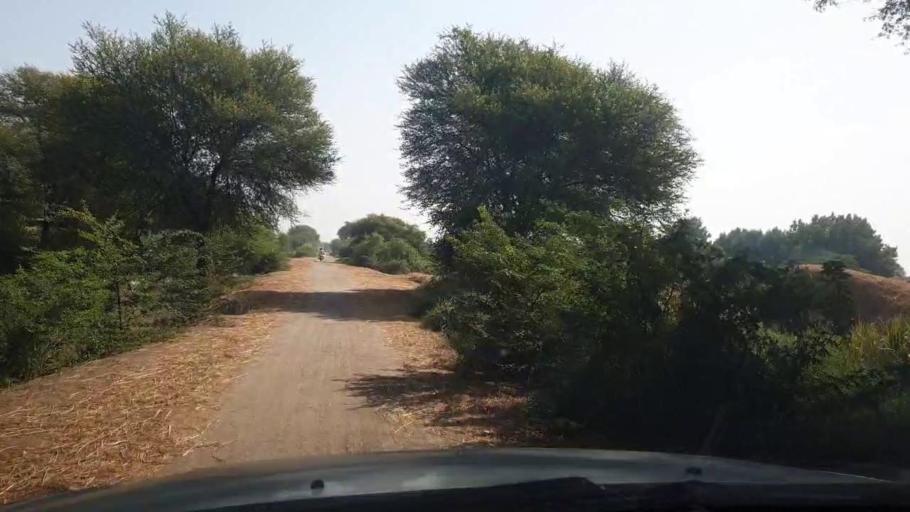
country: PK
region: Sindh
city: Bulri
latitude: 24.9119
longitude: 68.4497
